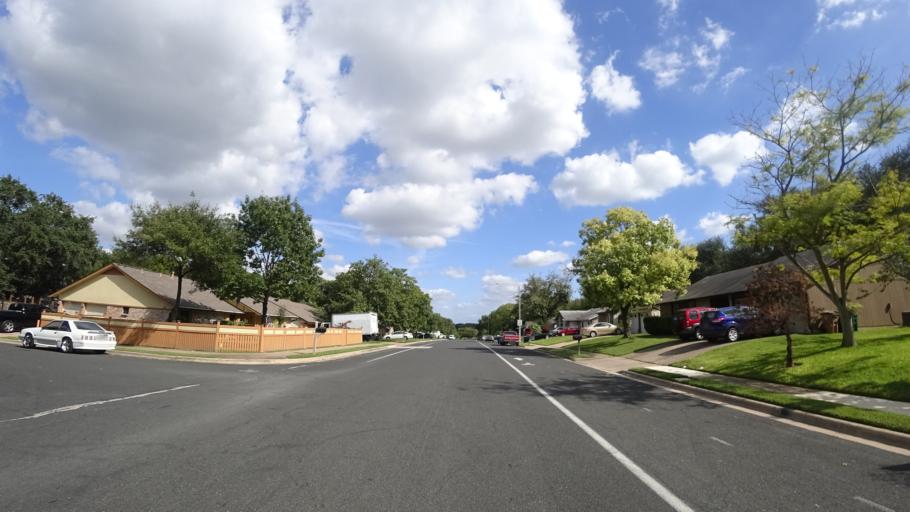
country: US
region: Texas
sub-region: Travis County
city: Onion Creek
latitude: 30.2030
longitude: -97.7915
